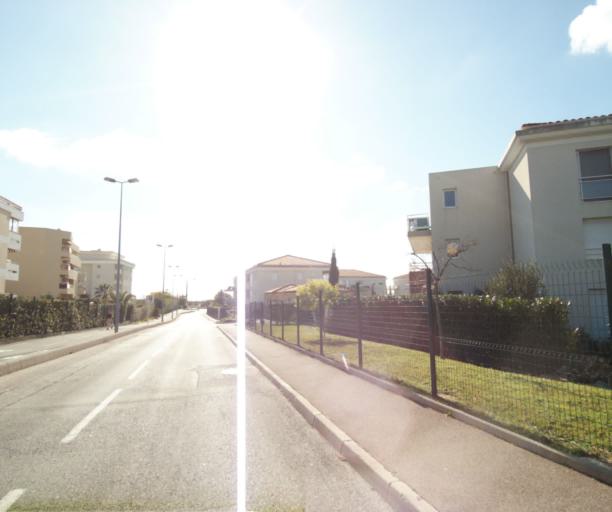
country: FR
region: Provence-Alpes-Cote d'Azur
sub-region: Departement des Alpes-Maritimes
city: Antibes
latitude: 43.5730
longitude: 7.0964
